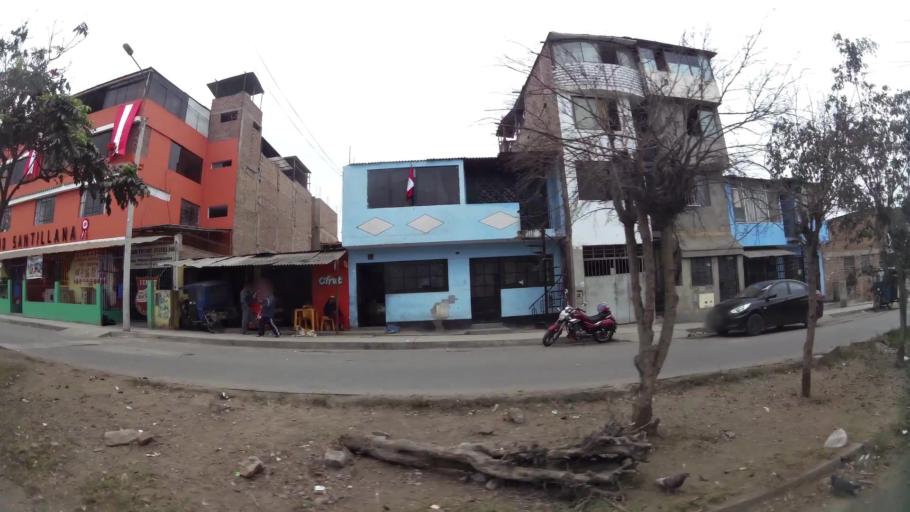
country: PE
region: Lima
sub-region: Lima
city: Surco
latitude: -12.1964
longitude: -76.9430
